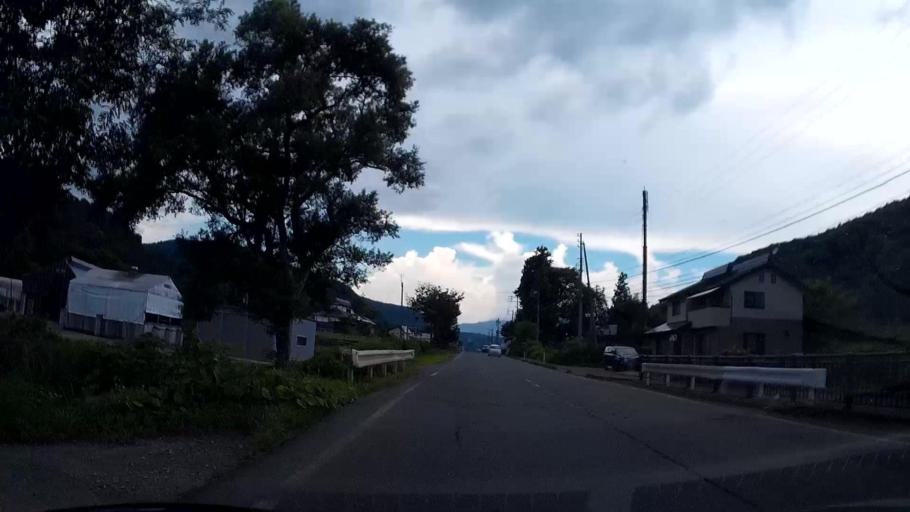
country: JP
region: Nagano
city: Iiyama
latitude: 36.9816
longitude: 138.5027
